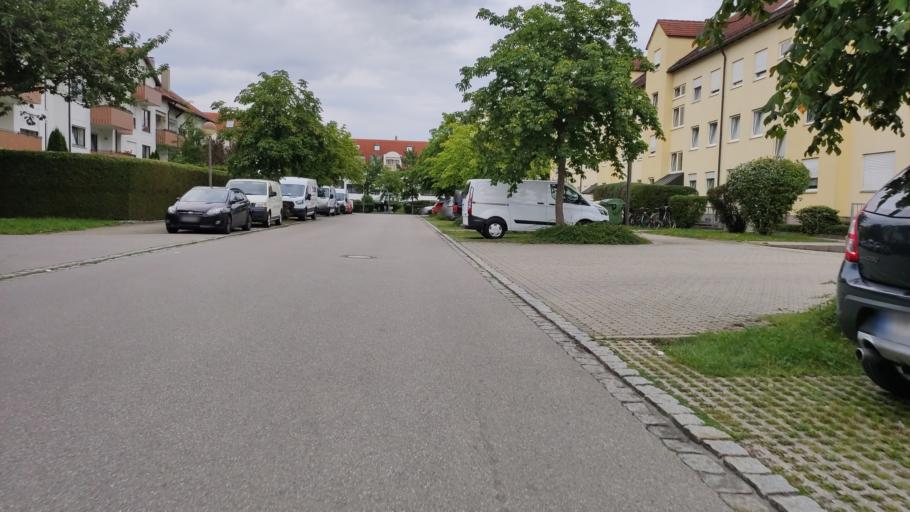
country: DE
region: Bavaria
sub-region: Swabia
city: Konigsbrunn
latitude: 48.2755
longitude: 10.8811
